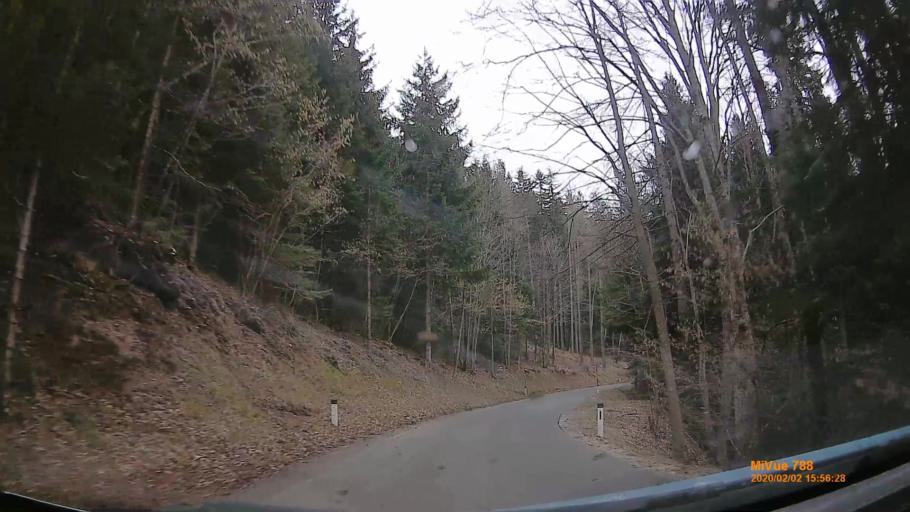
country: AT
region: Lower Austria
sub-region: Politischer Bezirk Neunkirchen
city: Semmering
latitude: 47.6669
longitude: 15.7855
